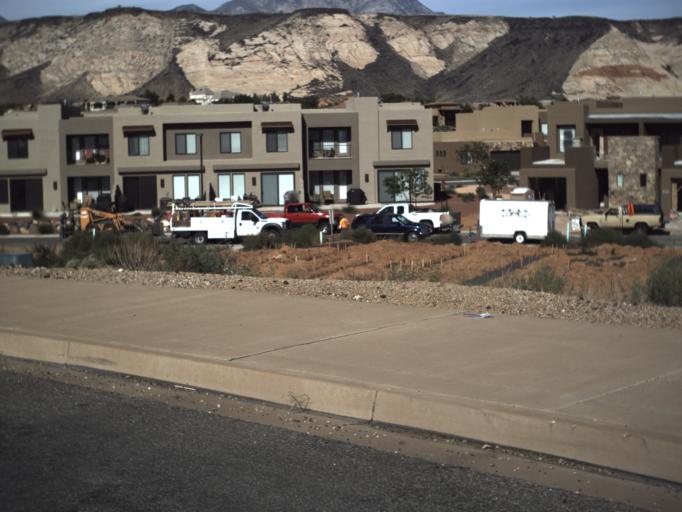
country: US
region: Utah
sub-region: Washington County
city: Ivins
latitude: 37.1948
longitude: -113.6215
